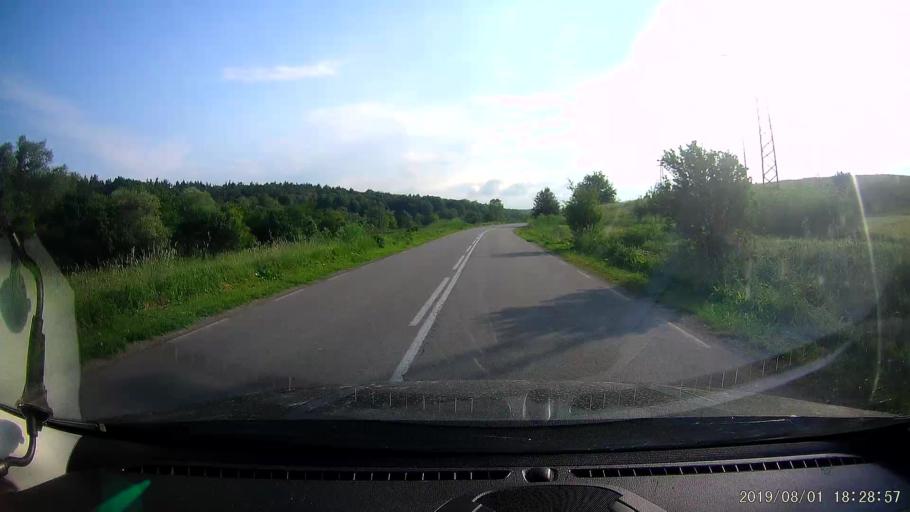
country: BG
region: Shumen
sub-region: Obshtina Venets
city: Venets
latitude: 43.5683
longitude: 26.9523
